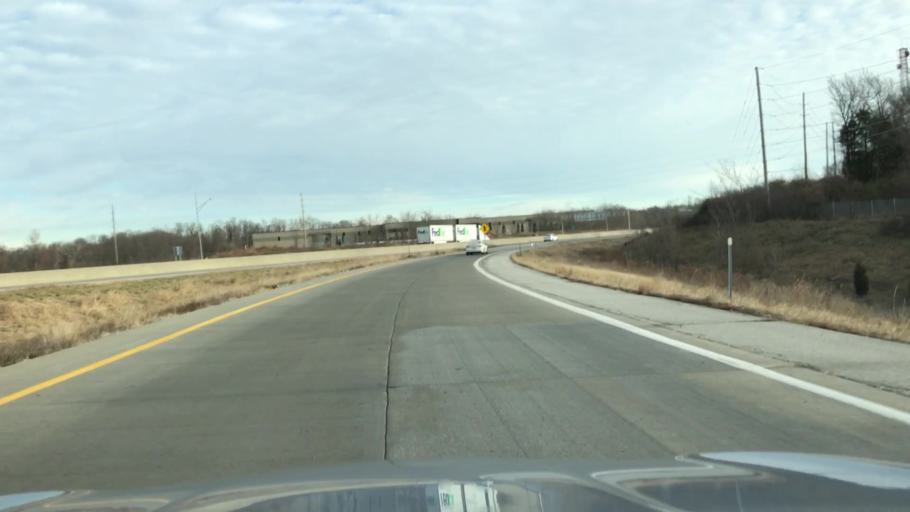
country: US
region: Missouri
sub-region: Jackson County
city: Lees Summit
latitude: 38.9359
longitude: -94.4008
